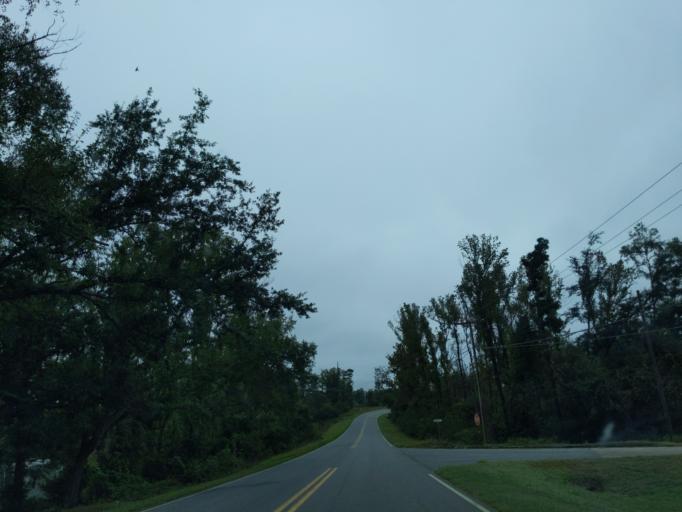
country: US
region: Florida
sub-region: Jackson County
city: Sneads
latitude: 30.7223
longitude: -84.9350
